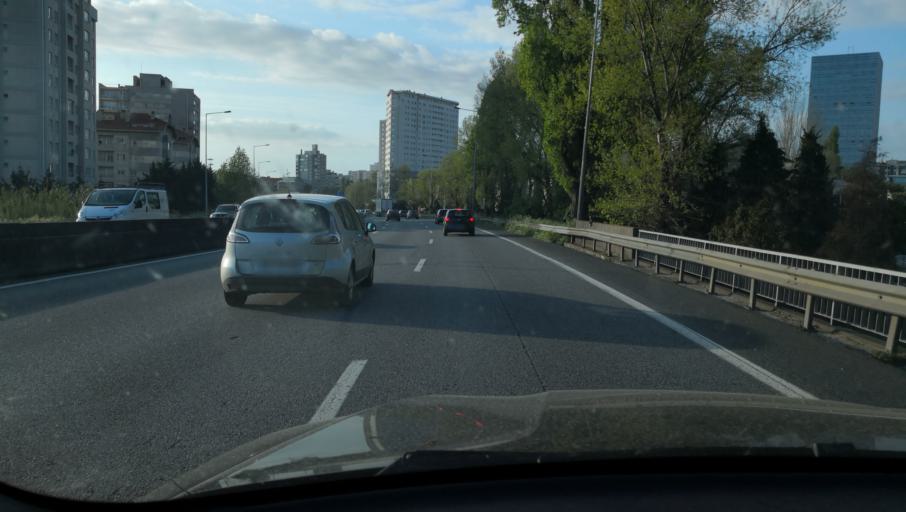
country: PT
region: Porto
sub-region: Matosinhos
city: Senhora da Hora
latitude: 41.1565
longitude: -8.6458
